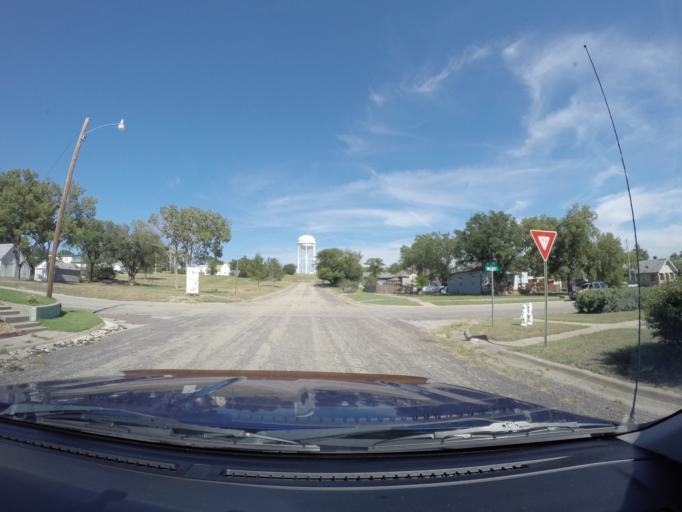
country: US
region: Kansas
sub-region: Rooks County
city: Stockton
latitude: 39.4412
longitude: -99.2738
